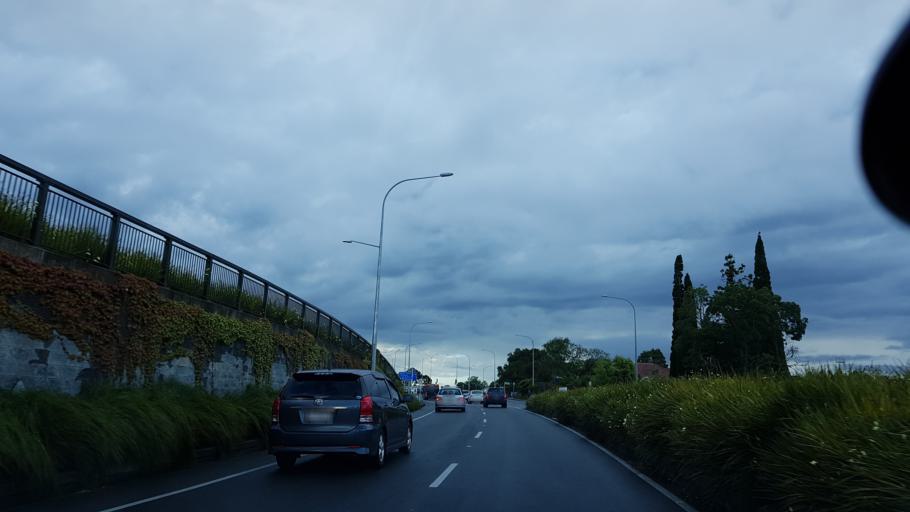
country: NZ
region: Auckland
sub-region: Auckland
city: North Shore
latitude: -36.7719
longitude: 174.7212
